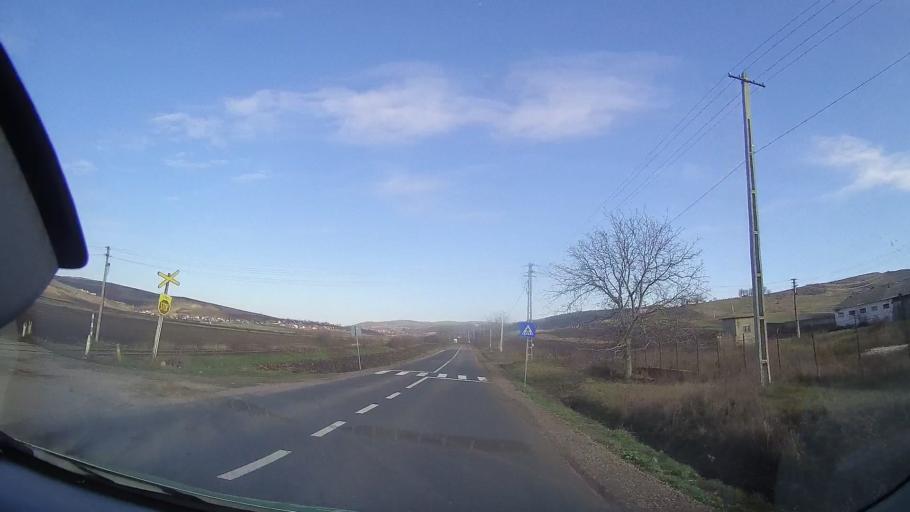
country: RO
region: Mures
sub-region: Comuna Zau De Campie
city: Zau de Campie
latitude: 46.5936
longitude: 24.1089
